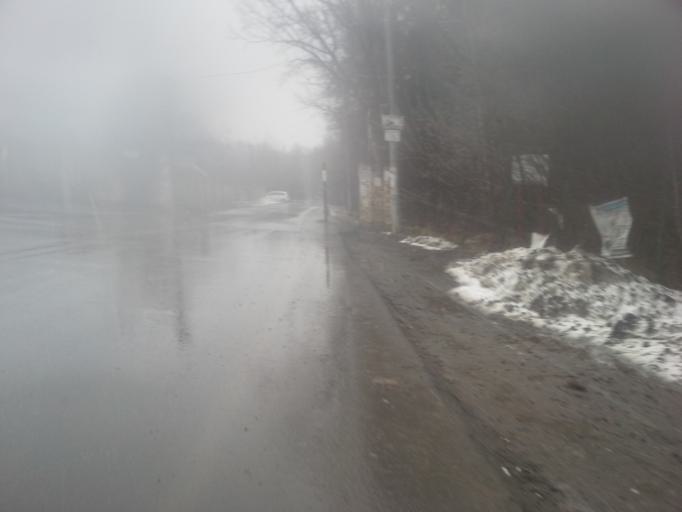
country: RU
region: Moskovskaya
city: Kommunarka
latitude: 55.5822
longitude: 37.4854
